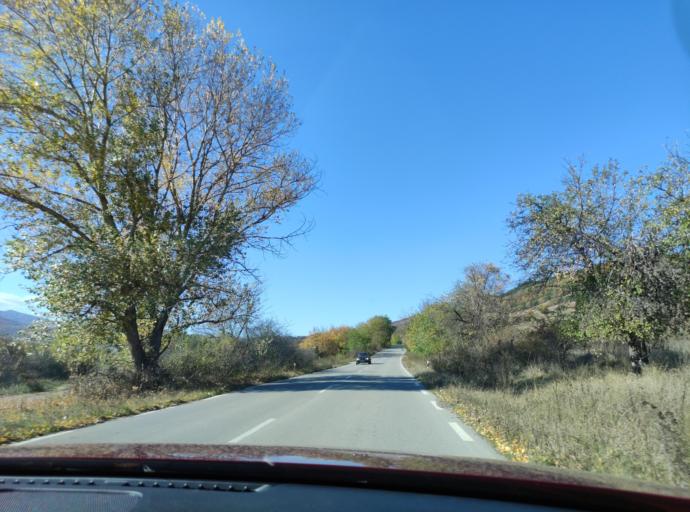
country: BG
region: Montana
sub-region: Obshtina Chiprovtsi
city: Chiprovtsi
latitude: 43.4303
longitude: 22.9940
